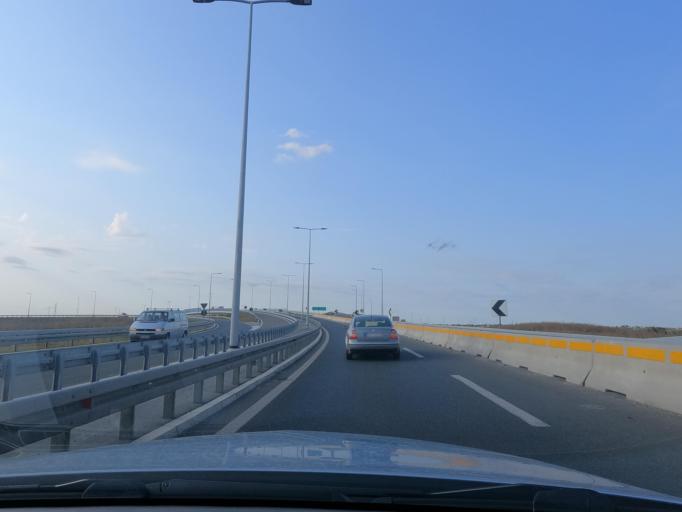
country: RS
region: Central Serbia
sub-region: Belgrade
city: Surcin
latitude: 44.7706
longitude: 20.2803
